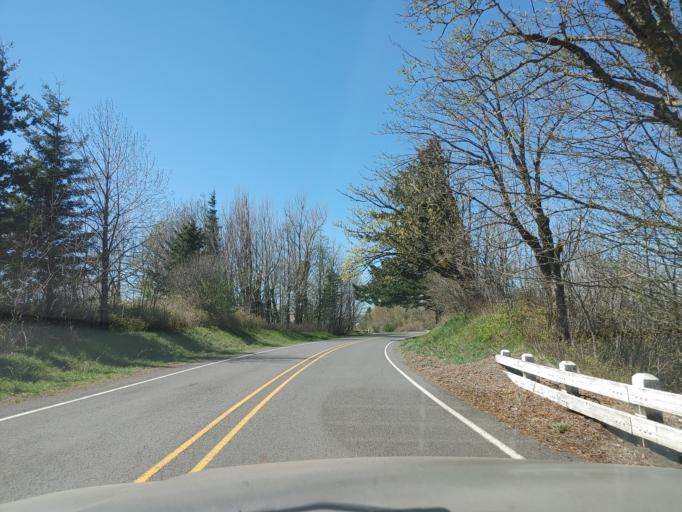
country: US
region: Washington
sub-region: Clark County
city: Washougal
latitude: 45.5318
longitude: -122.2575
